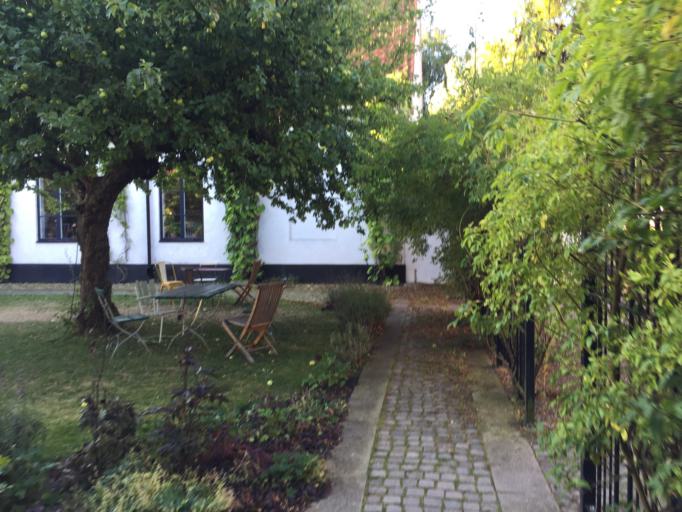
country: SE
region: Skane
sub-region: Ystads Kommun
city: Kopingebro
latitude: 55.4534
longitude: 14.1139
